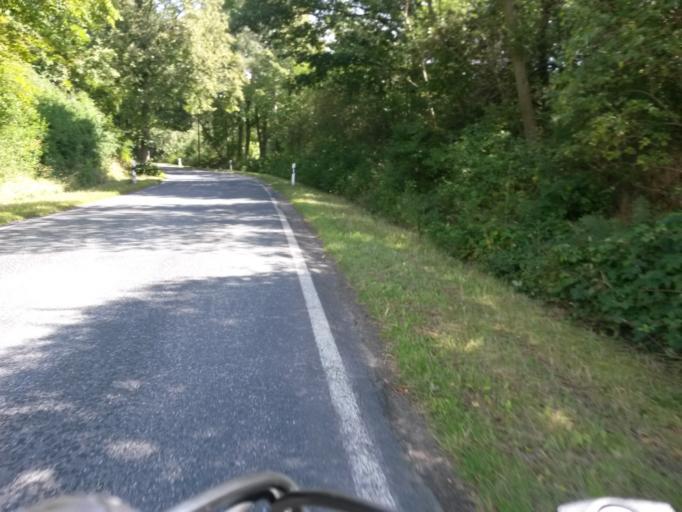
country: DE
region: Brandenburg
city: Angermunde
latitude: 53.0064
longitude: 13.9115
